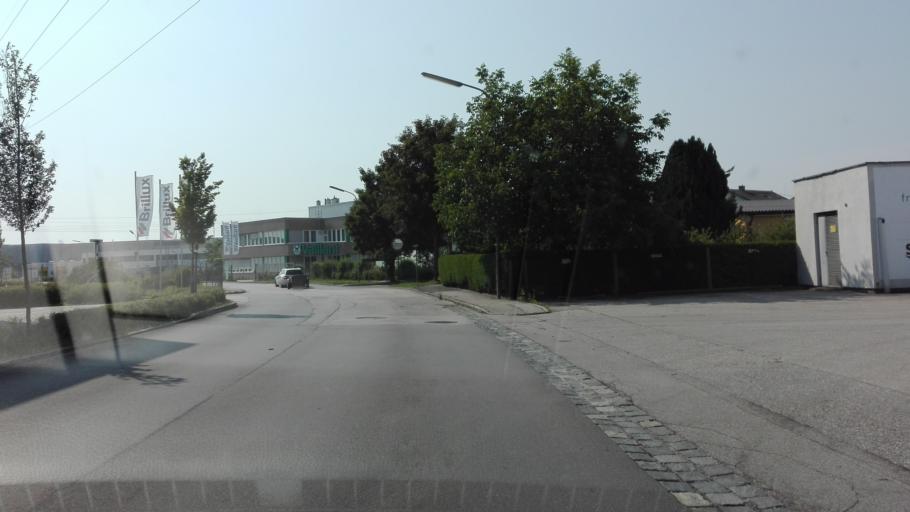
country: AT
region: Upper Austria
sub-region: Politischer Bezirk Linz-Land
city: Ansfelden
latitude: 48.2361
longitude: 14.2772
